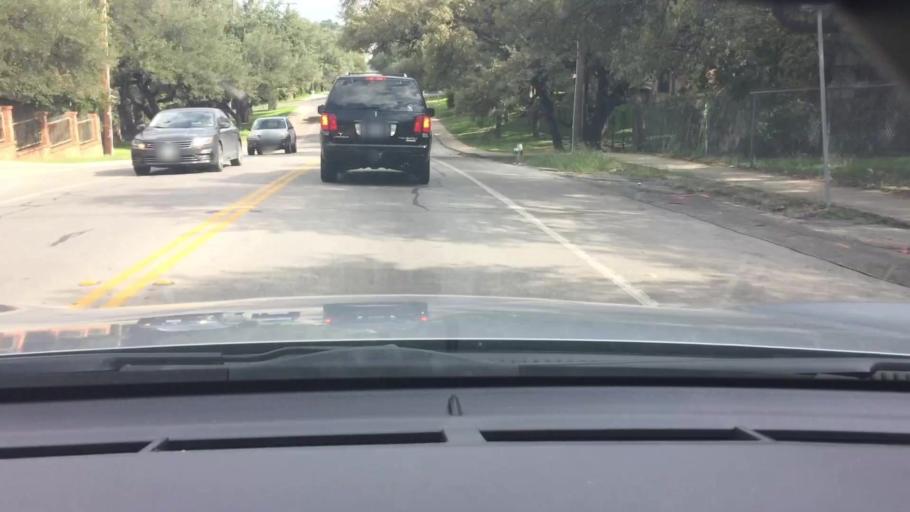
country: US
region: Texas
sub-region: Bexar County
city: Shavano Park
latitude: 29.5506
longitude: -98.5691
